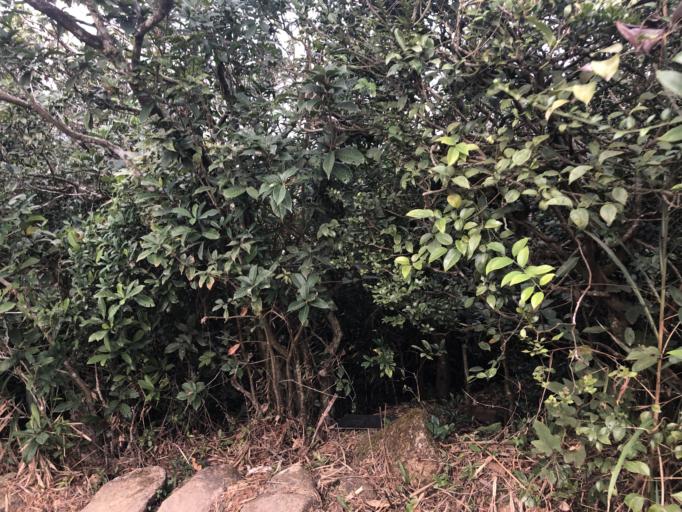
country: HK
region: Wanchai
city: Wan Chai
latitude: 22.2678
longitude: 114.2110
